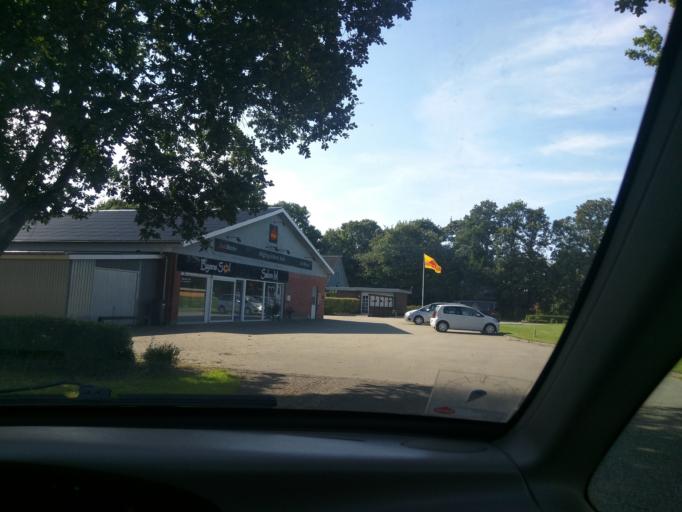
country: DK
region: Central Jutland
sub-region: Favrskov Kommune
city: Hammel
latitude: 56.2661
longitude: 9.7363
